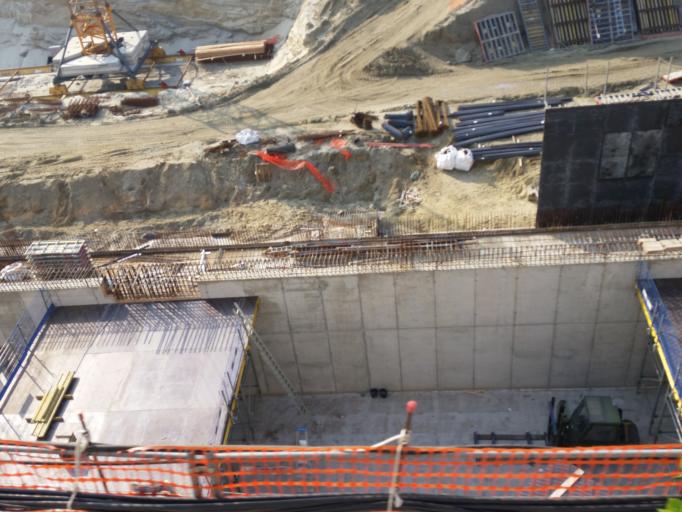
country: BE
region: Flanders
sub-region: Provincie Antwerpen
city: Mechelen
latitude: 51.0165
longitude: 4.4833
